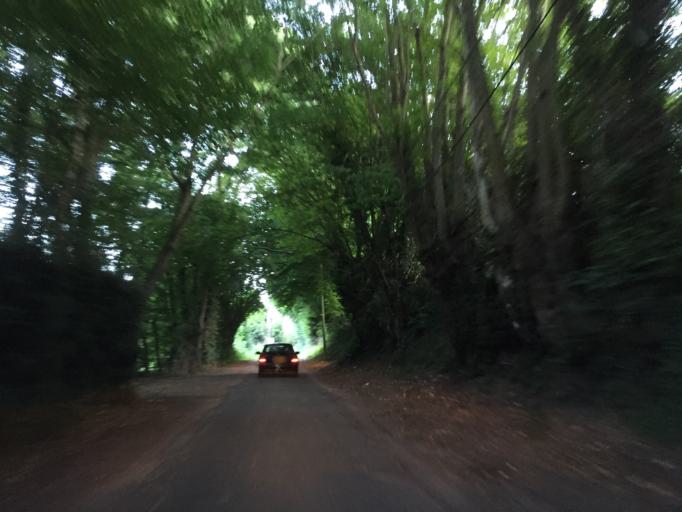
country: FR
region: Lower Normandy
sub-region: Departement du Calvados
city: Equemauville
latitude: 49.4160
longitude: 0.2018
